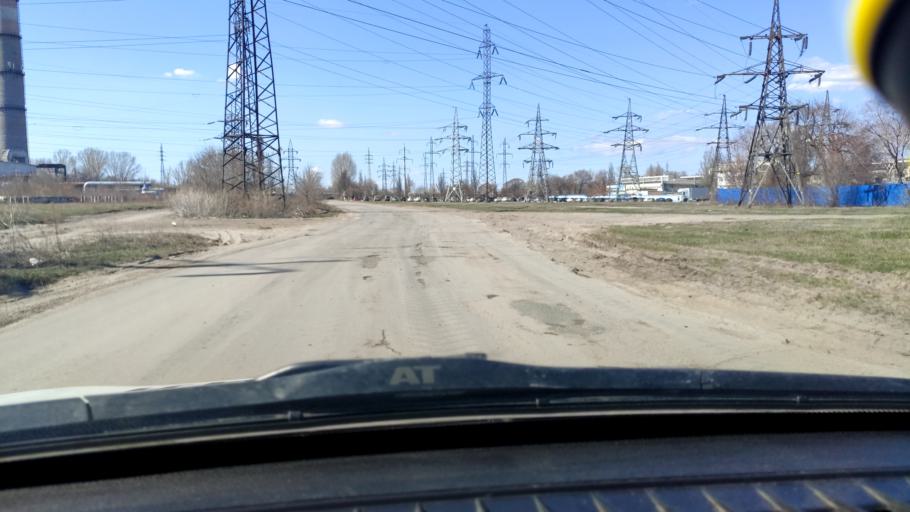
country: RU
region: Samara
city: Tol'yatti
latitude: 53.5502
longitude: 49.4548
